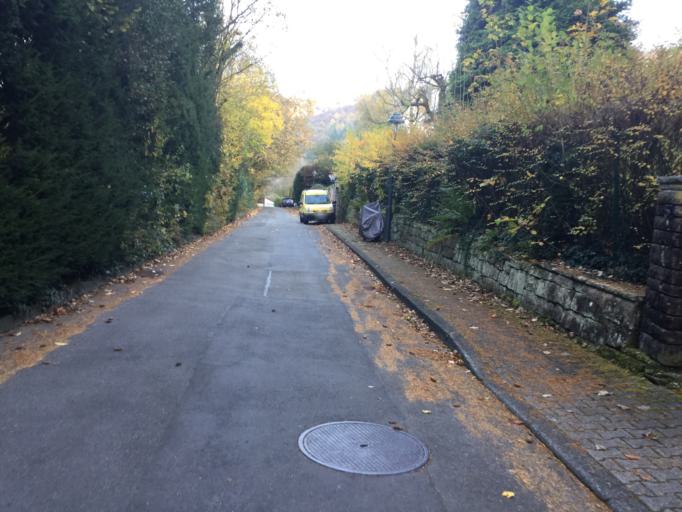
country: DE
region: Baden-Wuerttemberg
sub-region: Karlsruhe Region
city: Gaiberg
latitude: 49.4123
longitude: 8.7414
